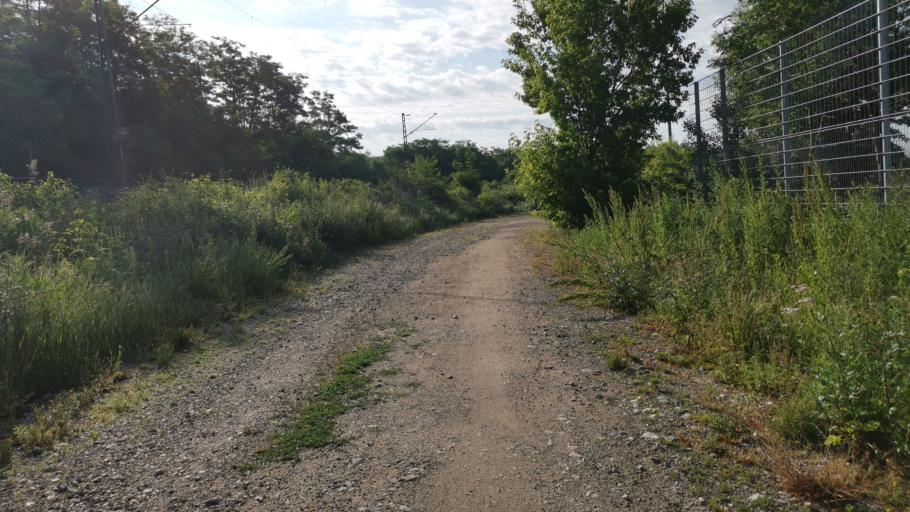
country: DE
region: Bavaria
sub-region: Regierungsbezirk Mittelfranken
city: Grossreuth bei Schweinau
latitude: 49.4226
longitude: 11.0496
